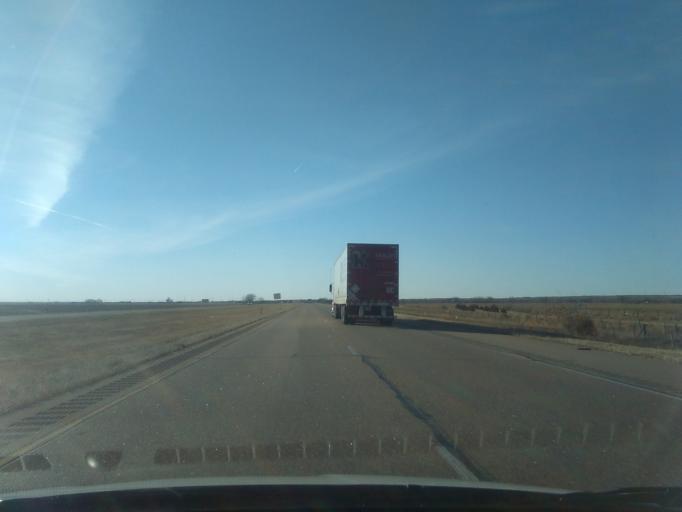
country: US
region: Colorado
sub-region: Sedgwick County
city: Julesburg
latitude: 41.0404
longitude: -102.1089
